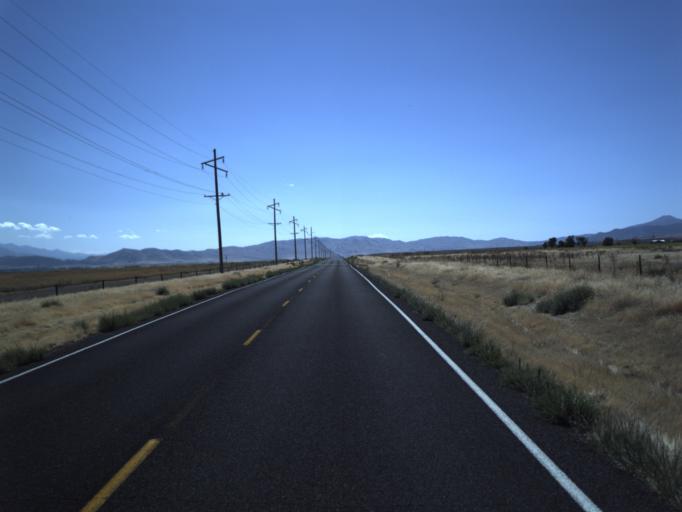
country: US
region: Utah
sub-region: Utah County
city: Genola
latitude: 40.0643
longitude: -111.9585
